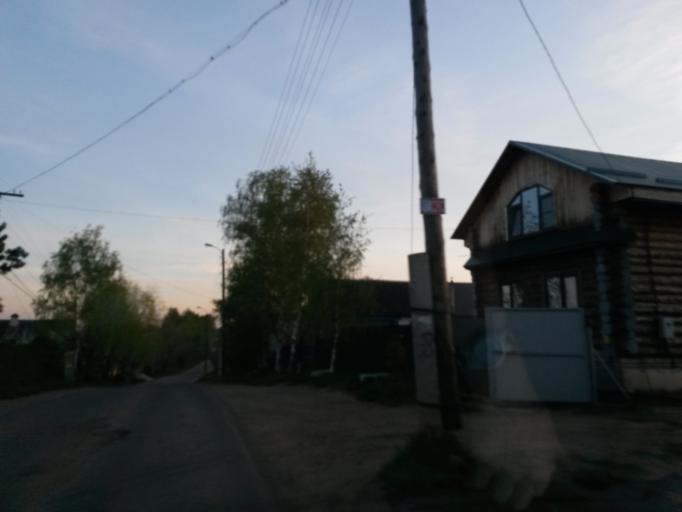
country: RU
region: Jaroslavl
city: Tutayev
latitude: 57.8899
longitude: 39.5561
